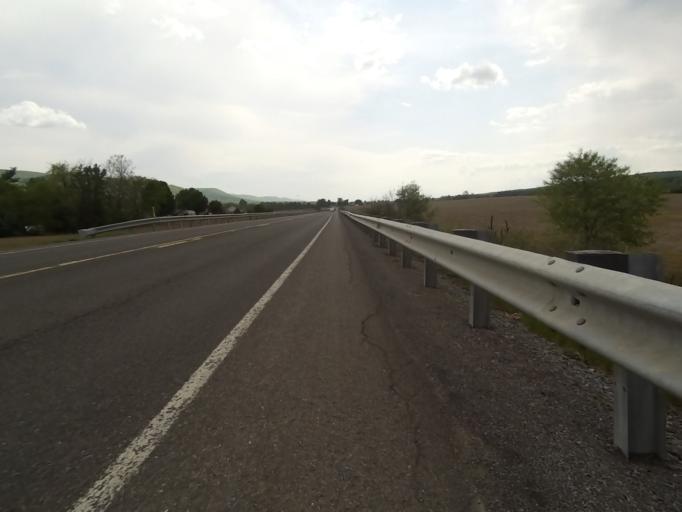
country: US
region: Pennsylvania
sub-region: Centre County
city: Zion
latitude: 40.9604
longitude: -77.6129
